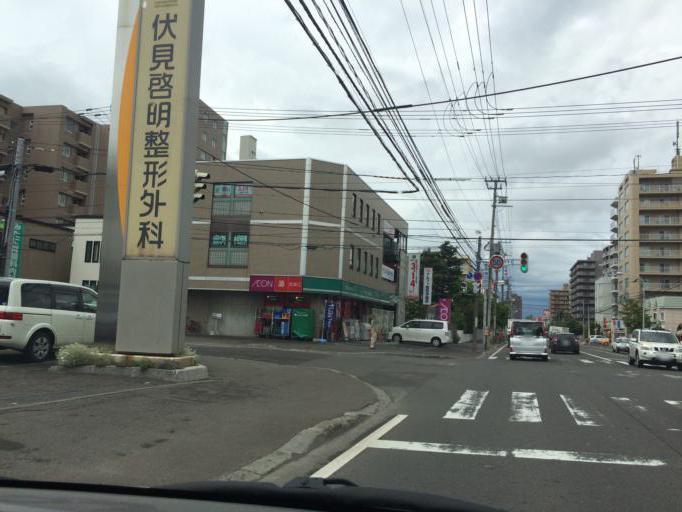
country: JP
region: Hokkaido
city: Sapporo
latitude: 43.0398
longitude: 141.3284
